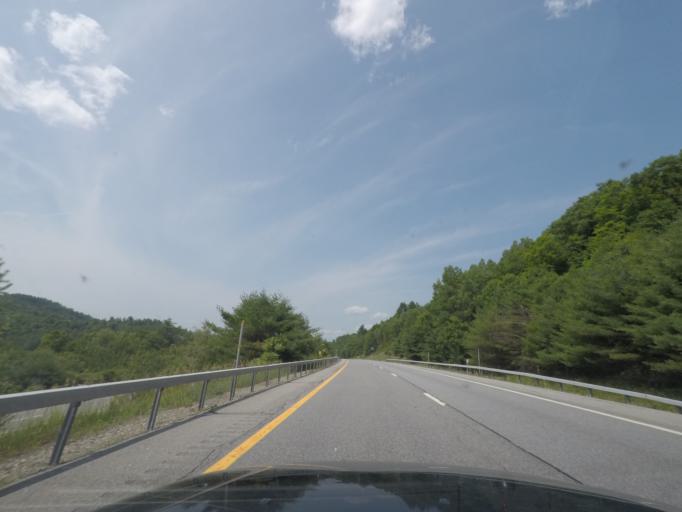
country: US
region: New York
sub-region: Warren County
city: Warrensburg
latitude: 43.5915
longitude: -73.7267
